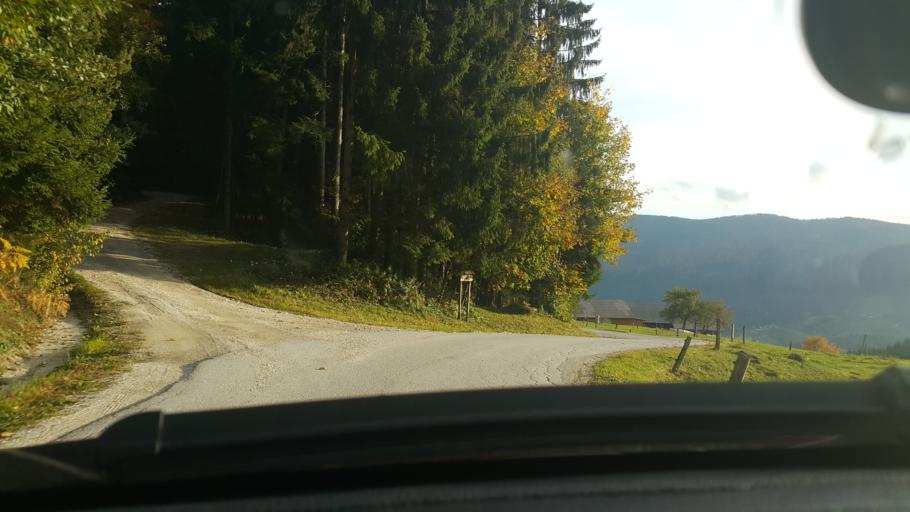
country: SI
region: Mislinja
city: Mislinja
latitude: 46.4296
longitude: 15.2587
